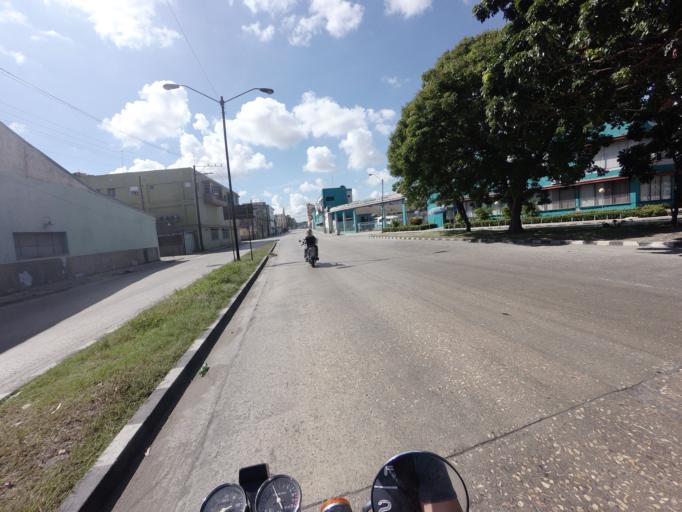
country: TM
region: Balkan
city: Gumdag
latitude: 38.8432
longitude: 54.1861
